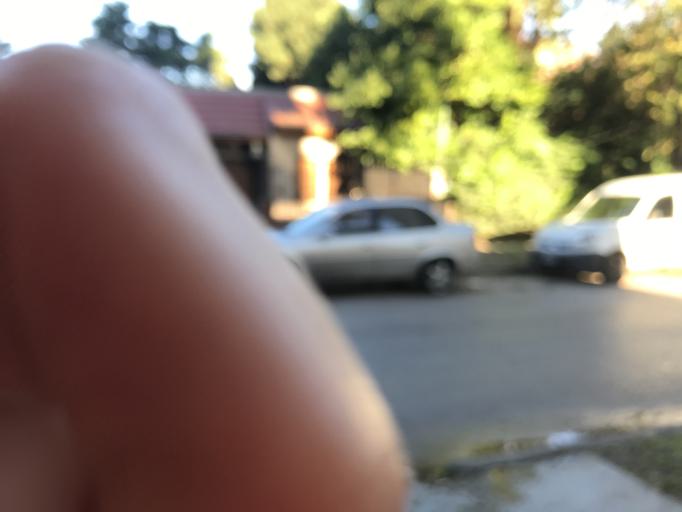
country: AR
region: Buenos Aires
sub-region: Partido de General San Martin
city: General San Martin
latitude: -34.5511
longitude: -58.5509
